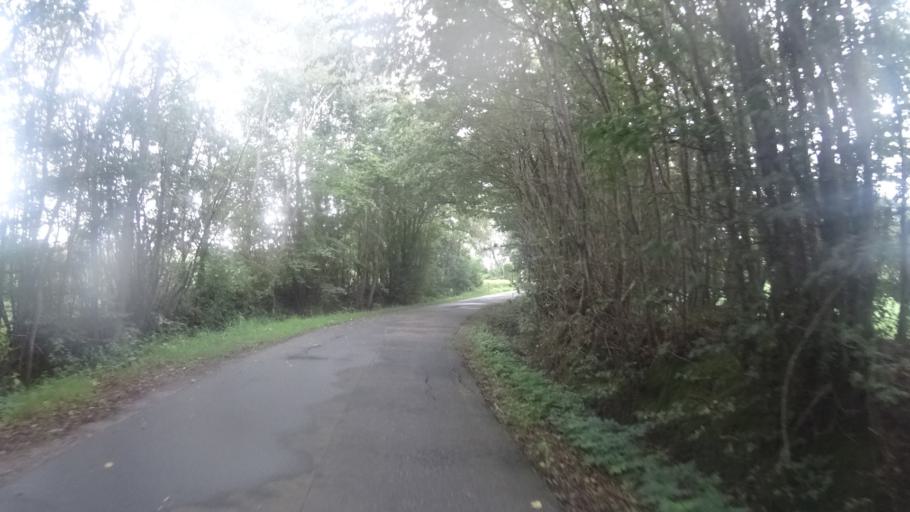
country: DE
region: Schleswig-Holstein
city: Hemdingen
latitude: 53.7635
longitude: 9.8219
